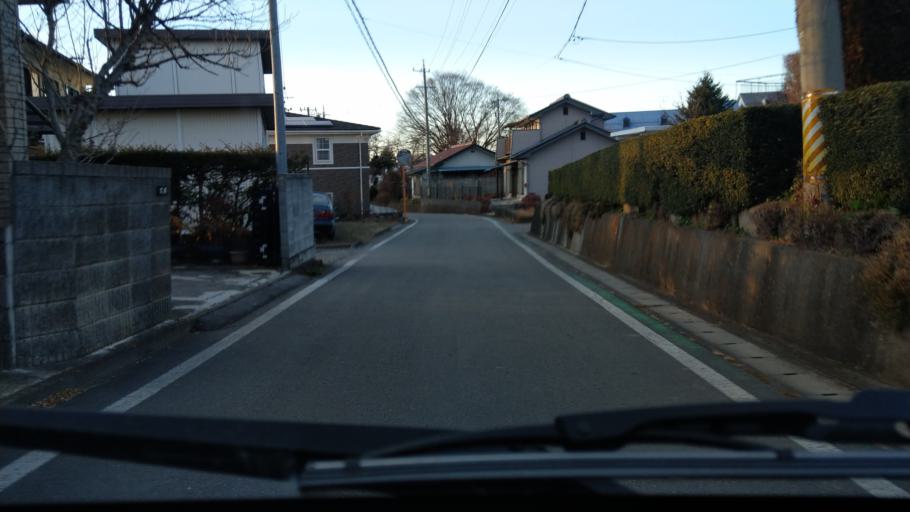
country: JP
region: Nagano
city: Komoro
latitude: 36.3438
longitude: 138.3894
